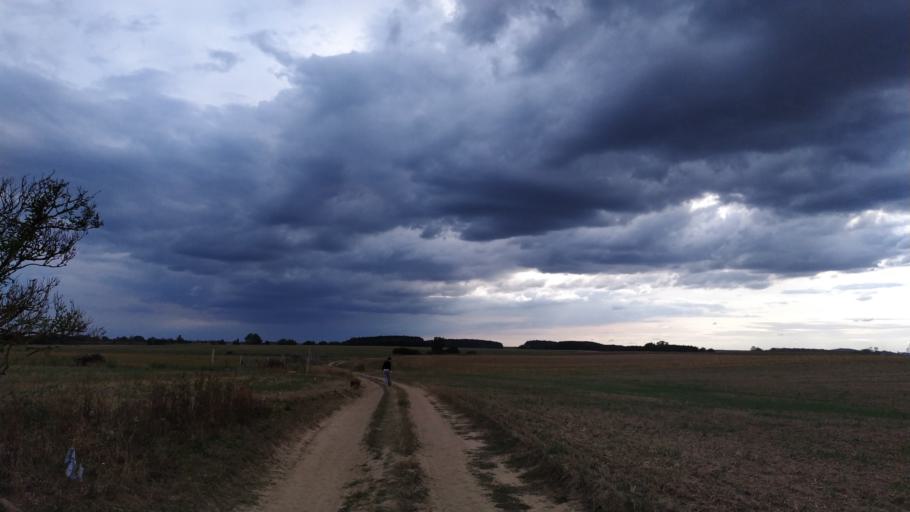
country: DE
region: Mecklenburg-Vorpommern
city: Wolgast
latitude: 54.0548
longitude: 13.8228
